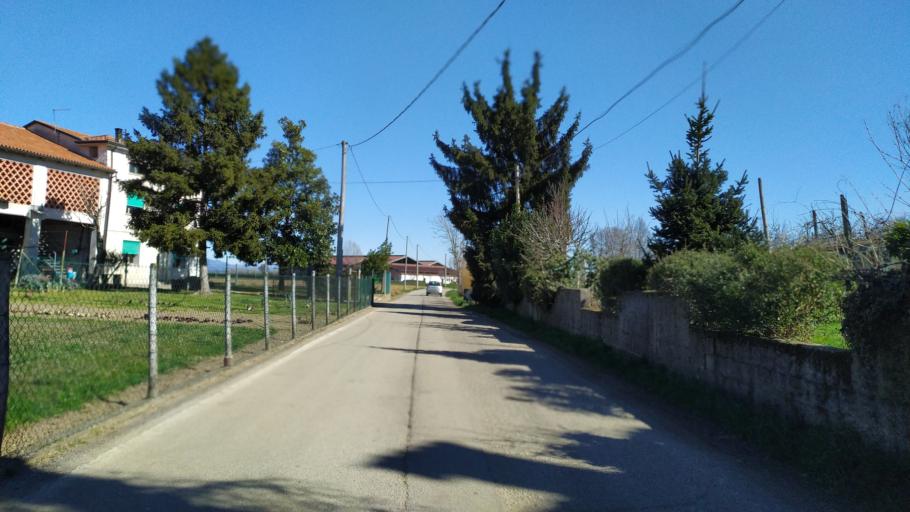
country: IT
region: Veneto
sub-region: Provincia di Vicenza
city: Vigardolo
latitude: 45.6231
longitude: 11.5862
